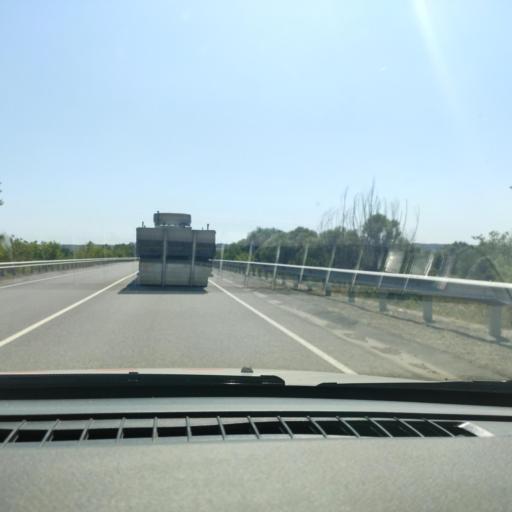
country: RU
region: Voronezj
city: Ostrogozhsk
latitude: 50.8627
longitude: 39.1246
